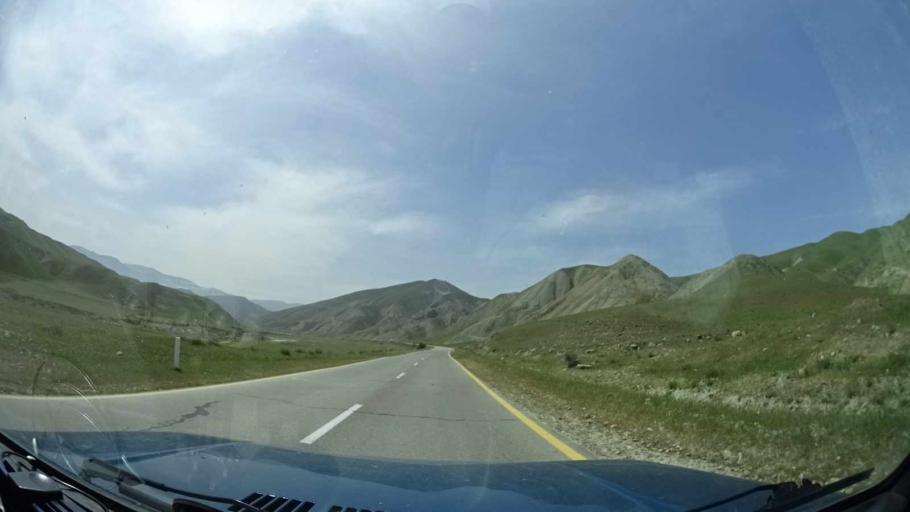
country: AZ
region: Xizi
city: Kilyazi
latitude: 40.8554
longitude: 49.2836
